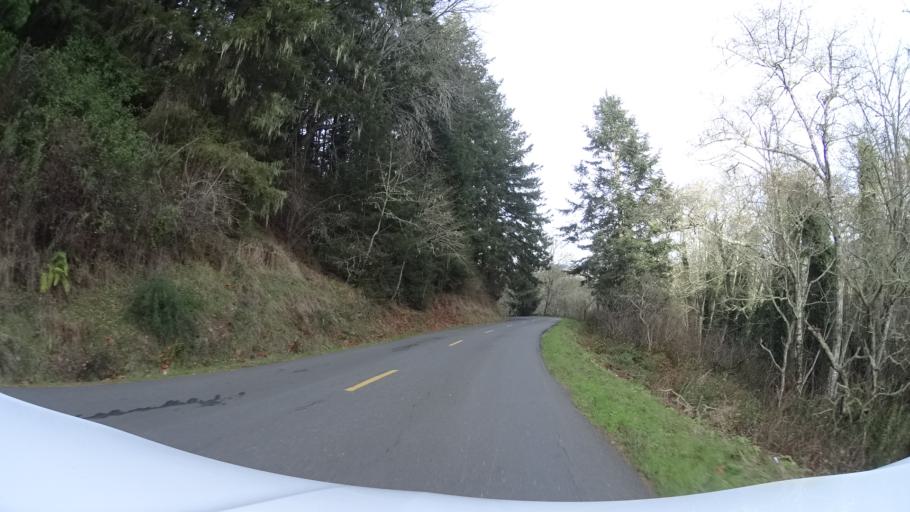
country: US
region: California
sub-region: Humboldt County
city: Ferndale
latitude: 40.5687
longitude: -124.2706
